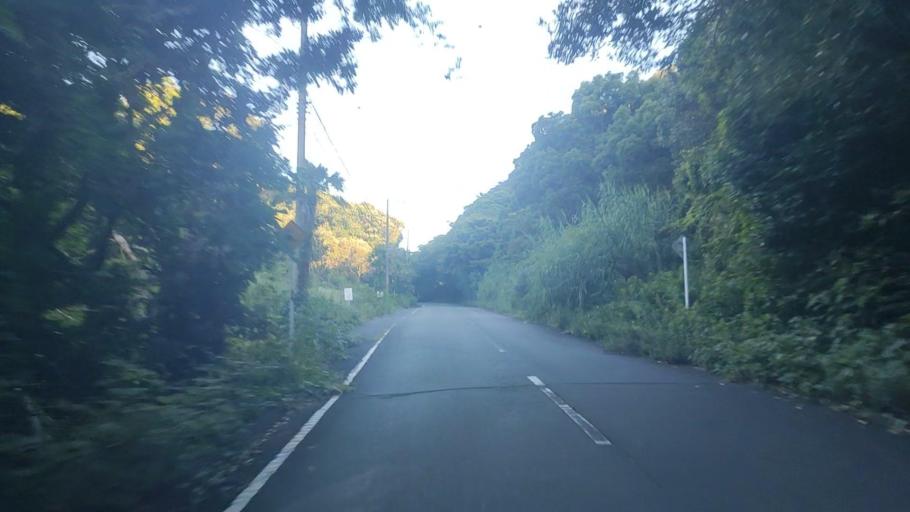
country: JP
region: Mie
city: Ise
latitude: 34.2676
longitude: 136.7691
